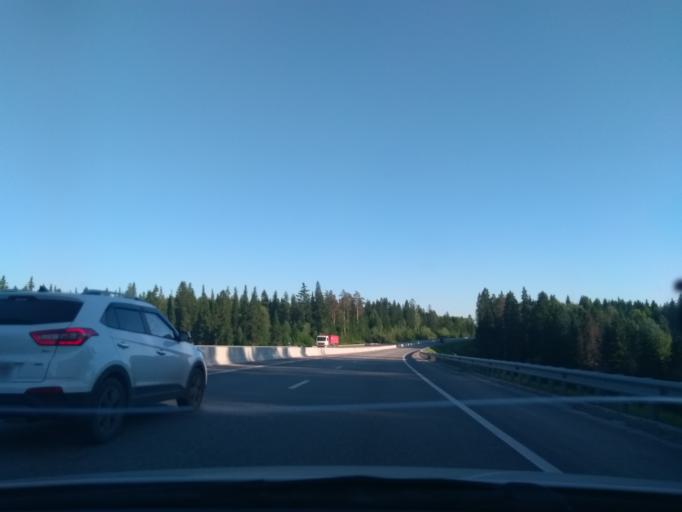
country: RU
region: Perm
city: Ferma
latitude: 57.9718
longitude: 56.4021
